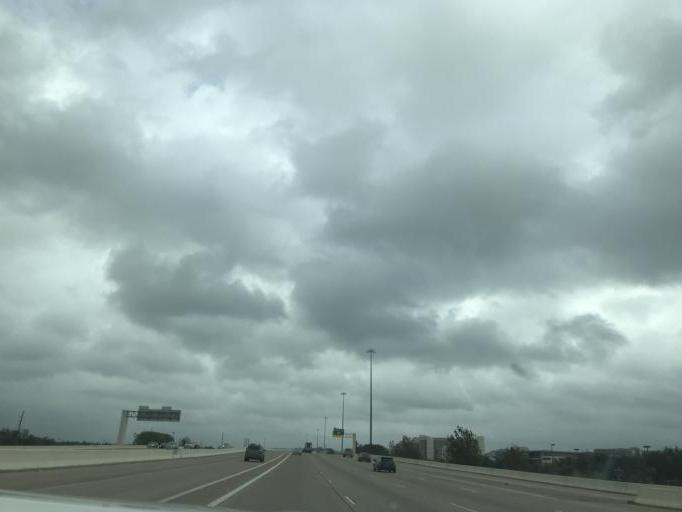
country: US
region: Texas
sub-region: Fort Bend County
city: Sugar Land
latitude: 29.5876
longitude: -95.6373
